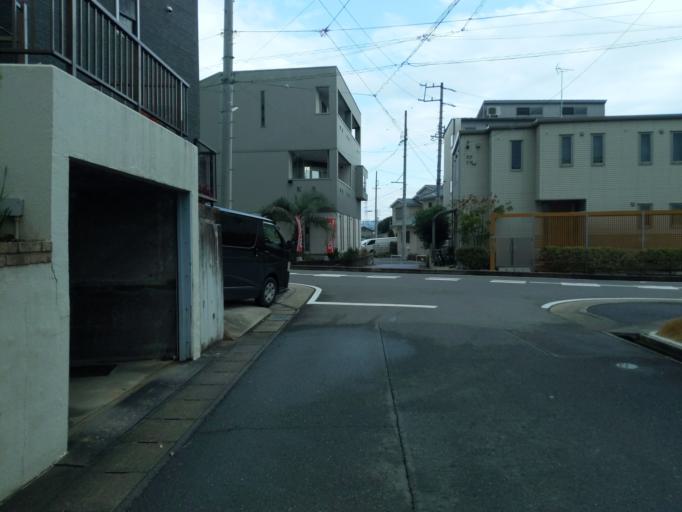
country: JP
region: Aichi
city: Kasugai
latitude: 35.2588
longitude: 136.9917
